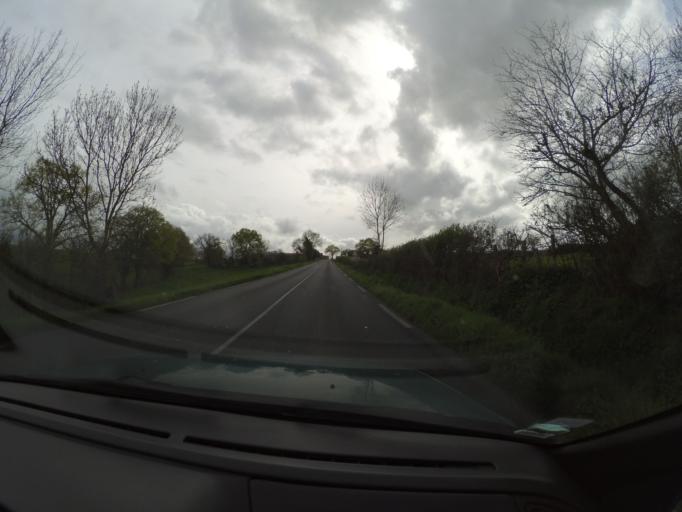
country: FR
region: Pays de la Loire
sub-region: Departement de Maine-et-Loire
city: Saint-Laurent-des-Autels
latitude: 47.2991
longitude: -1.1672
